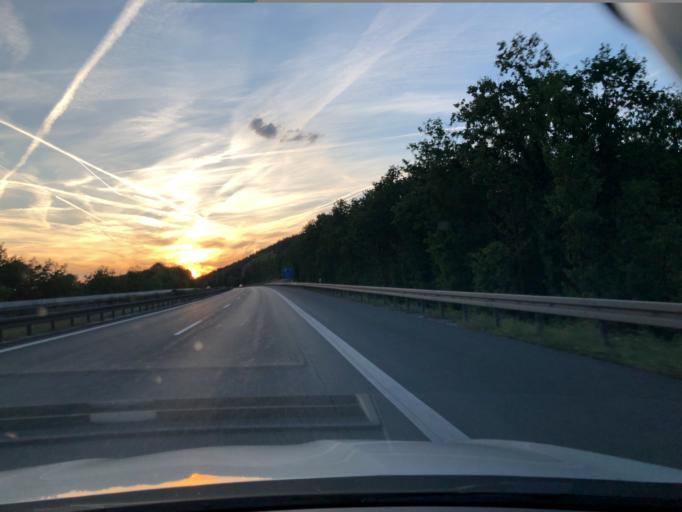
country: DE
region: Bavaria
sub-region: Regierungsbezirk Mittelfranken
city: Altdorf
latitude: 49.4037
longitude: 11.3682
